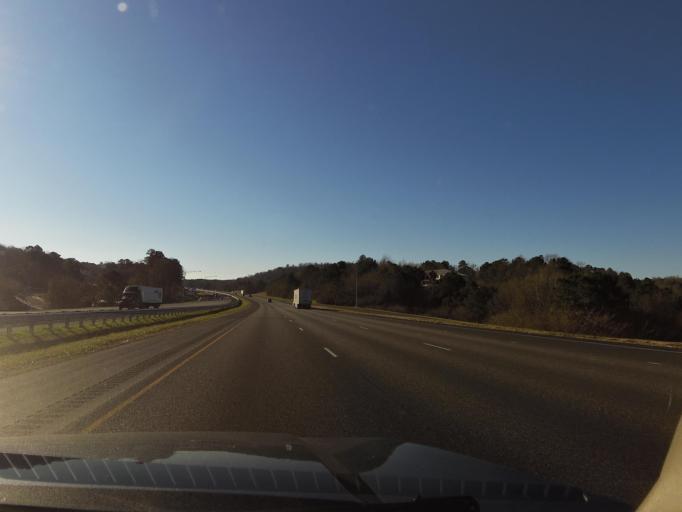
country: US
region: Alabama
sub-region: Jefferson County
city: Gardendale
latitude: 33.6483
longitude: -86.8295
